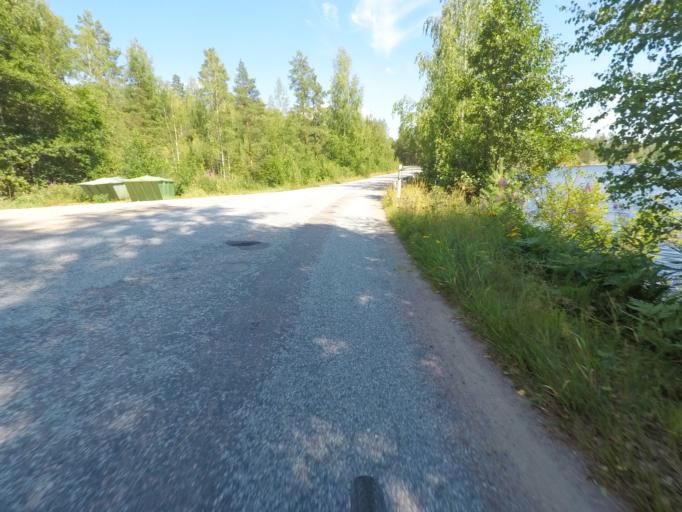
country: FI
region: Southern Savonia
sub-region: Mikkeli
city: Puumala
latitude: 61.4214
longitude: 28.0937
